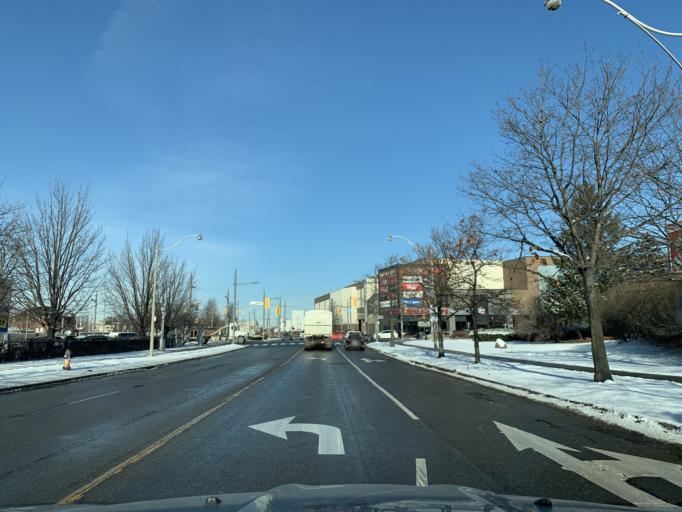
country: CA
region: Ontario
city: Toronto
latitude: 43.6710
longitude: -79.4707
